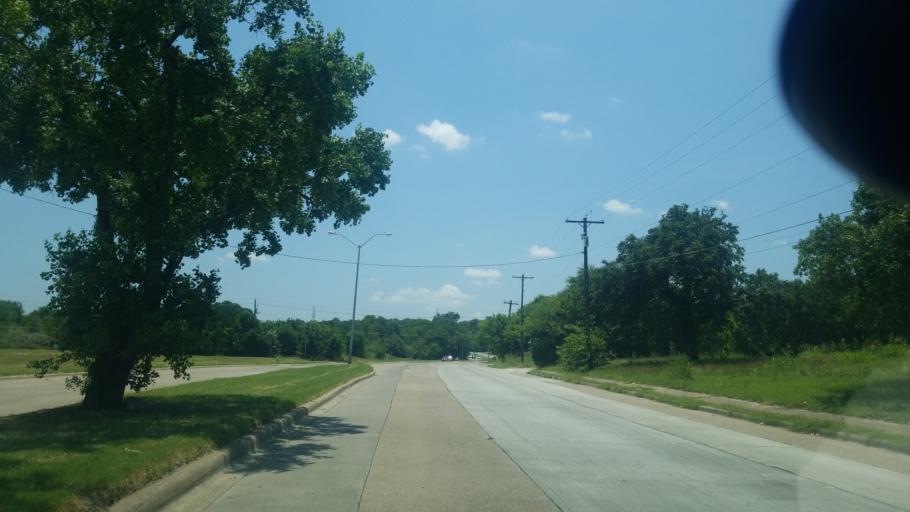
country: US
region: Texas
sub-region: Dallas County
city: Dallas
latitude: 32.7308
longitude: -96.7852
